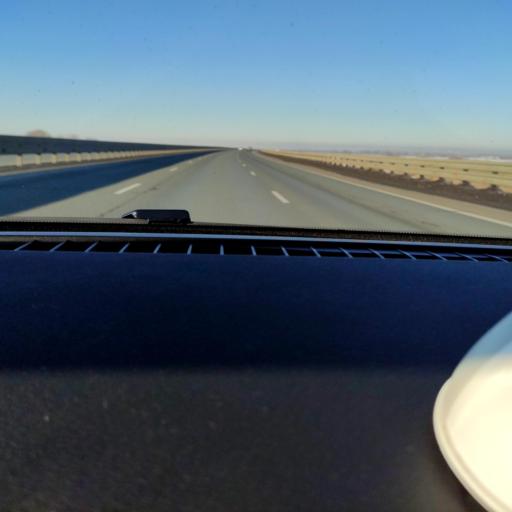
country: RU
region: Samara
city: Smyshlyayevka
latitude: 53.1508
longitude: 50.3595
